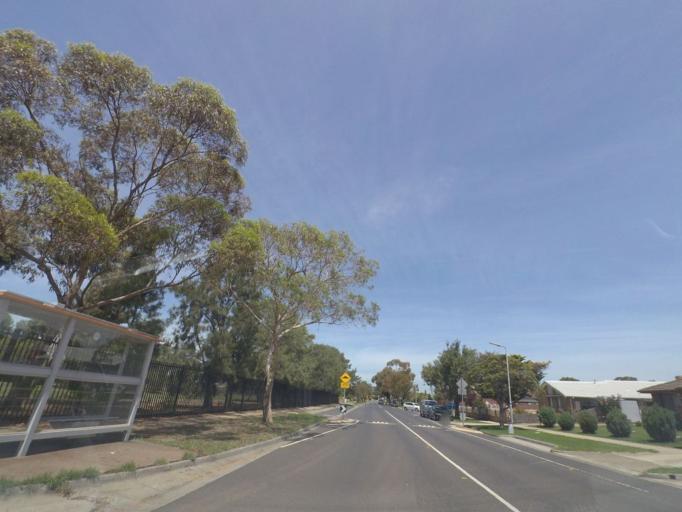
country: AU
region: Victoria
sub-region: Brimbank
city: Keilor Downs
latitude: -37.7166
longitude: 144.8116
